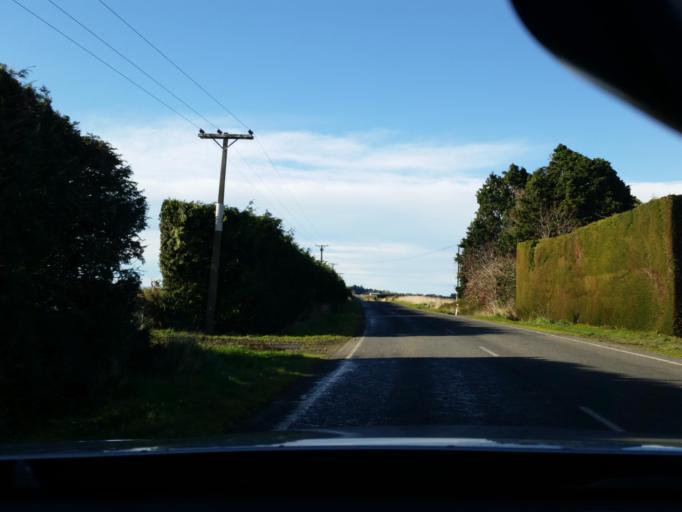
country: NZ
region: Southland
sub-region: Southland District
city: Riverton
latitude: -46.1540
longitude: 168.0470
